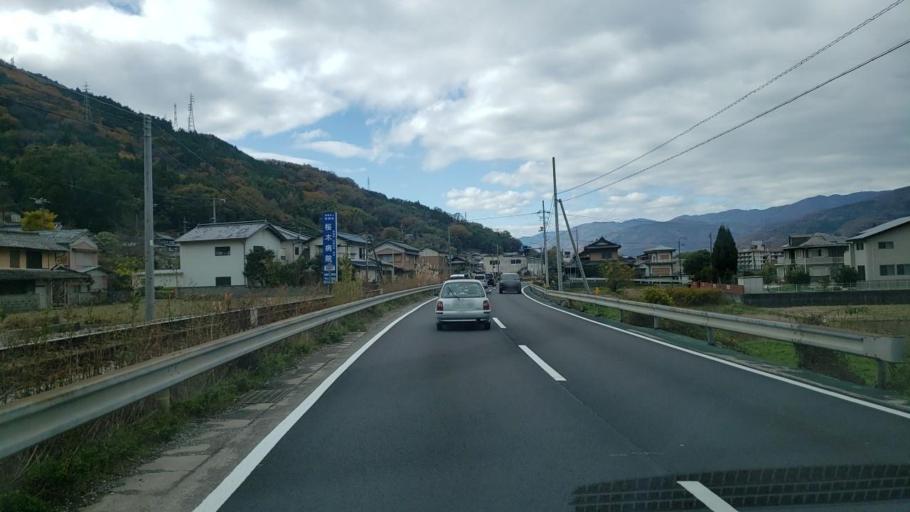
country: JP
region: Tokushima
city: Wakimachi
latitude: 34.0533
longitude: 134.1458
